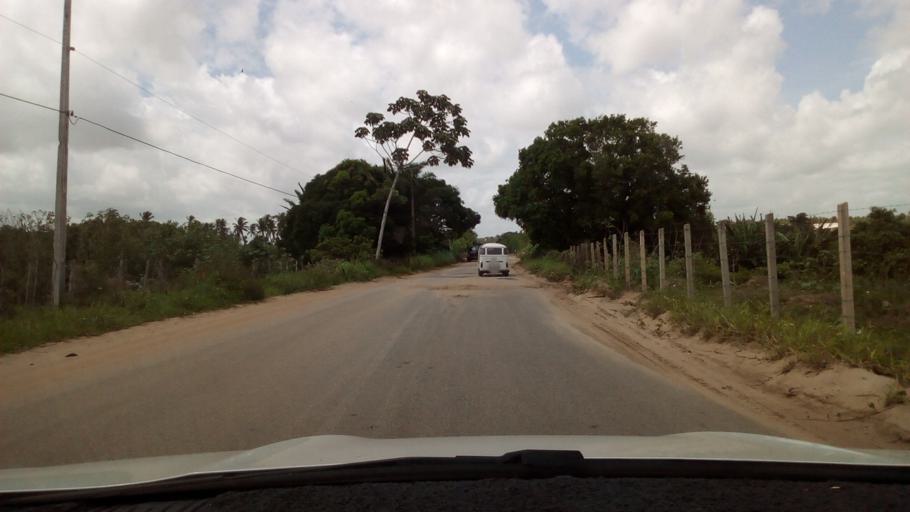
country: BR
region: Paraiba
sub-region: Alhandra
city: Alhandra
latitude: -7.4620
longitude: -34.9163
